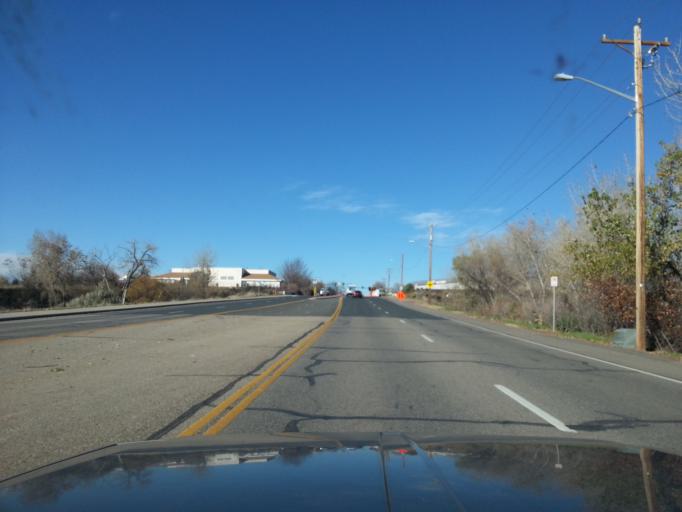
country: US
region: Colorado
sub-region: Larimer County
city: Loveland
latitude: 40.4009
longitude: -105.1105
